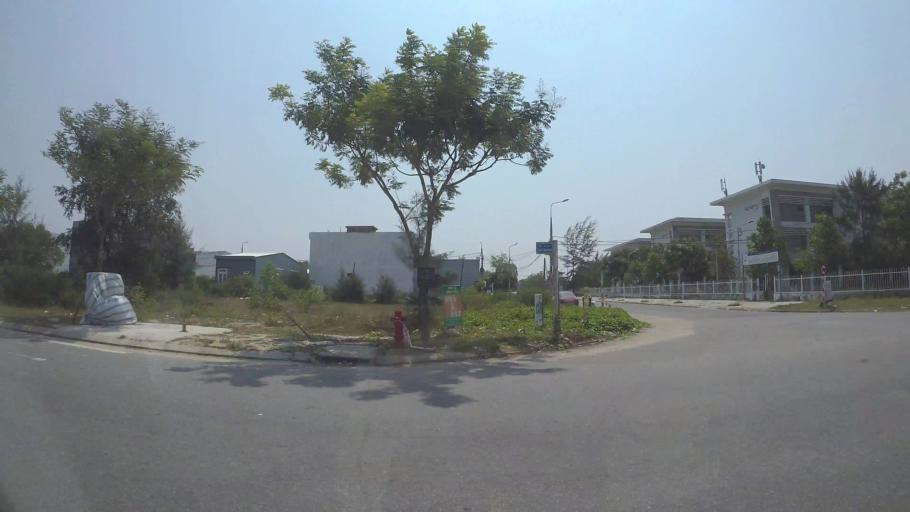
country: VN
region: Da Nang
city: Ngu Hanh Son
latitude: 15.9779
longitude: 108.2591
